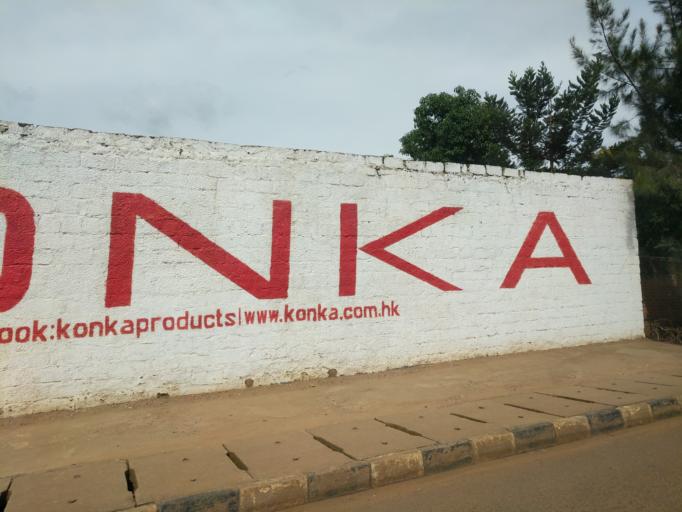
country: RW
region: Kigali
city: Kigali
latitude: -1.9709
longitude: 30.1314
